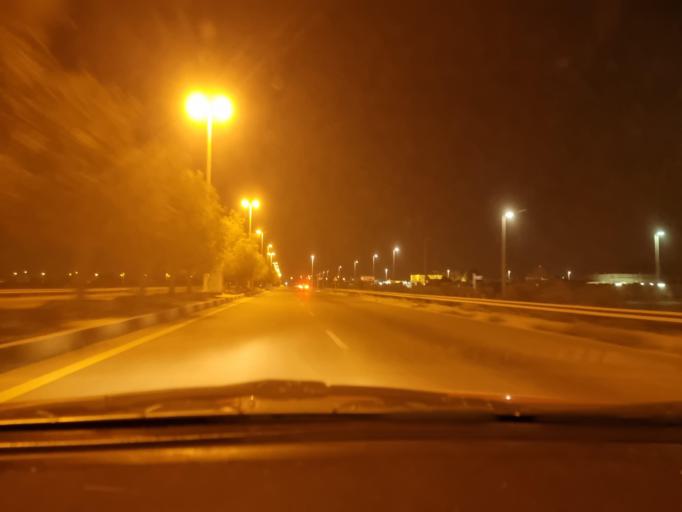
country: AE
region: Abu Dhabi
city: Abu Dhabi
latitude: 24.3830
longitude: 54.6850
